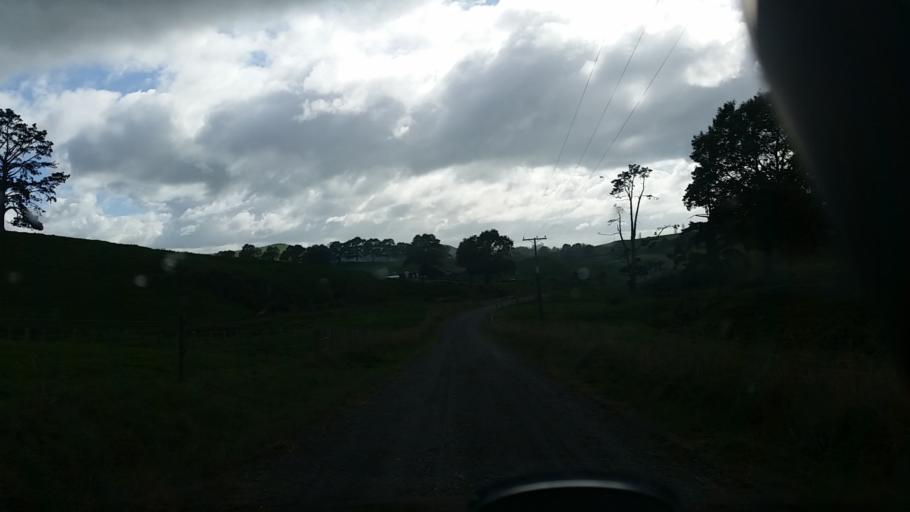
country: NZ
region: Waikato
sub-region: Matamata-Piako District
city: Matamata
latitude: -37.8171
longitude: 175.6739
